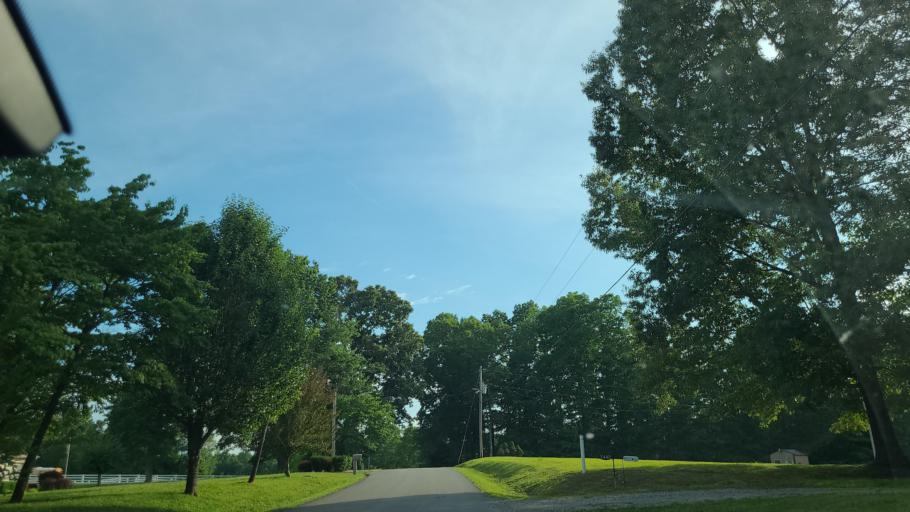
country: US
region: Kentucky
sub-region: Whitley County
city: Corbin
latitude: 36.8934
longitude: -84.2319
